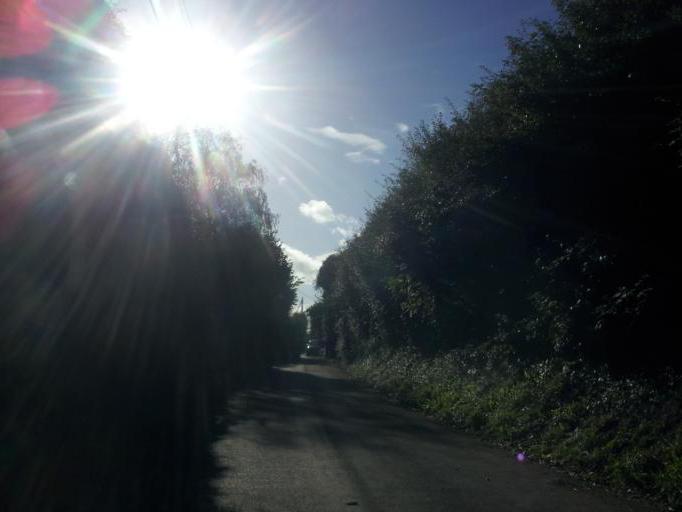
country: GB
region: England
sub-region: Kent
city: Rainham
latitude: 51.3840
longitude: 0.5916
